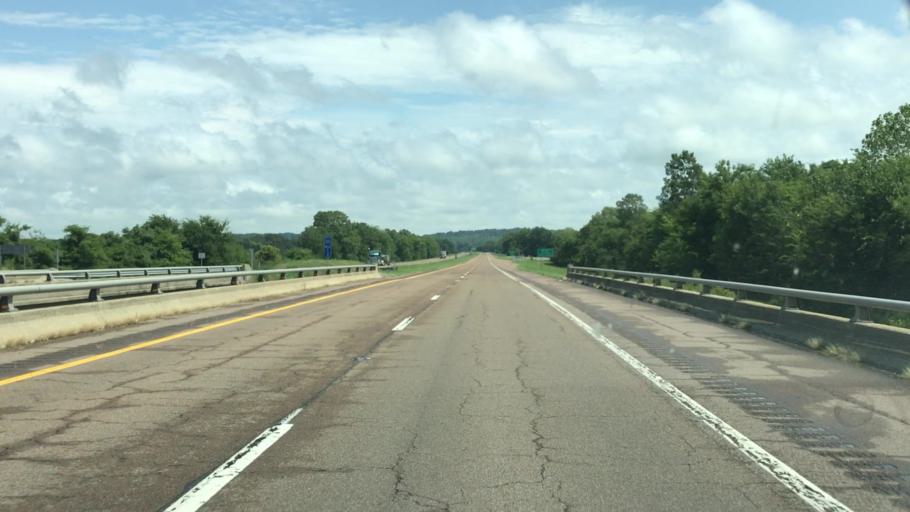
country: US
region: Tennessee
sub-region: Dyer County
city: Dyersburg
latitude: 36.0808
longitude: -89.5301
